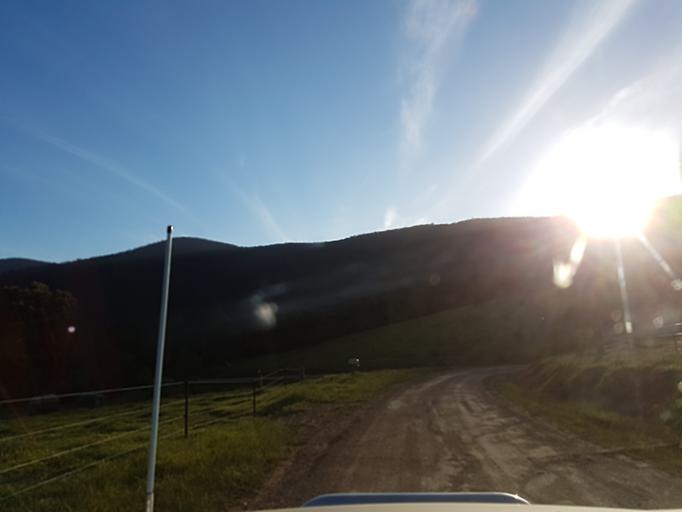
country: AU
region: Victoria
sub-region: East Gippsland
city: Bairnsdale
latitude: -37.4125
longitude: 147.1218
